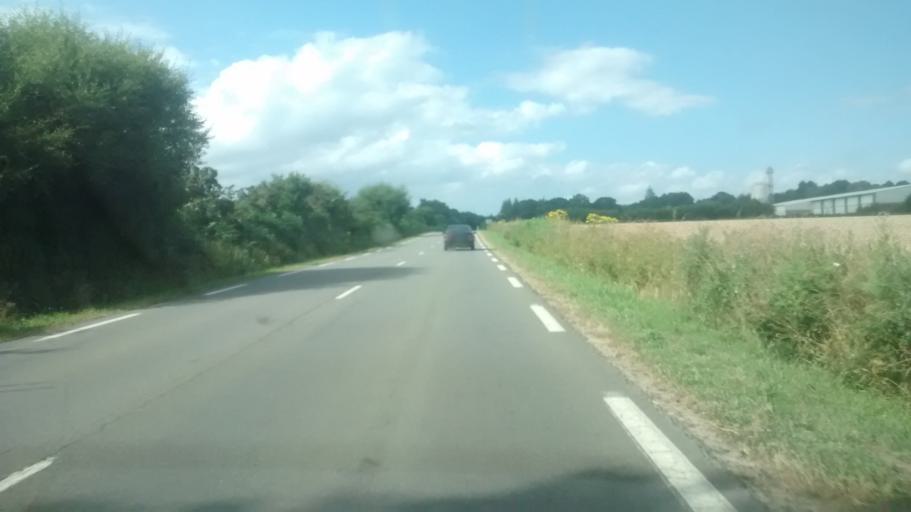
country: FR
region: Brittany
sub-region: Departement d'Ille-et-Vilaine
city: Saint-Meen-le-Grand
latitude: 48.2191
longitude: -2.1771
